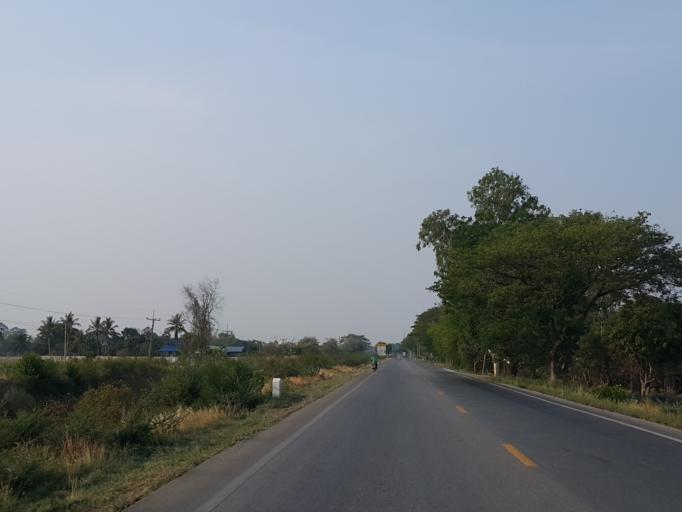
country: TH
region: Chai Nat
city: Sankhaburi
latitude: 15.0355
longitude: 100.1455
